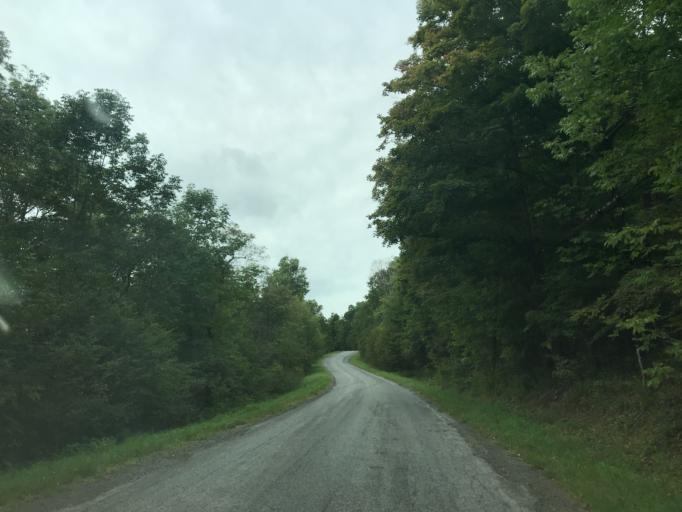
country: US
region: New York
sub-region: Delaware County
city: Stamford
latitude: 42.5142
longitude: -74.6608
